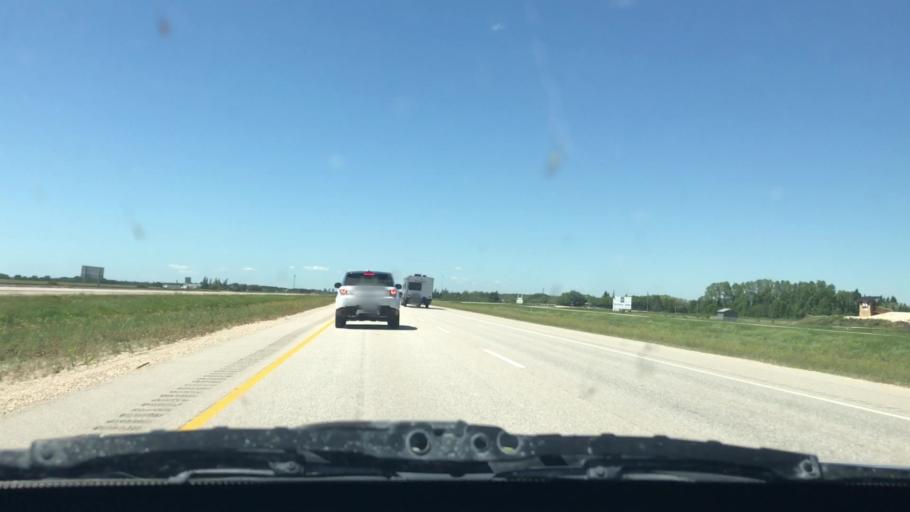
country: CA
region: Manitoba
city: Niverville
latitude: 49.8090
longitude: -96.9082
